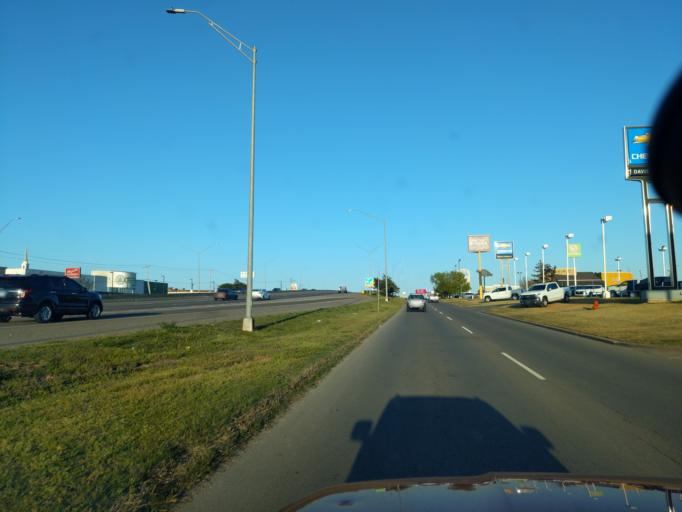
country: US
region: Oklahoma
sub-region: Cleveland County
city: Moore
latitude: 35.3911
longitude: -97.5248
